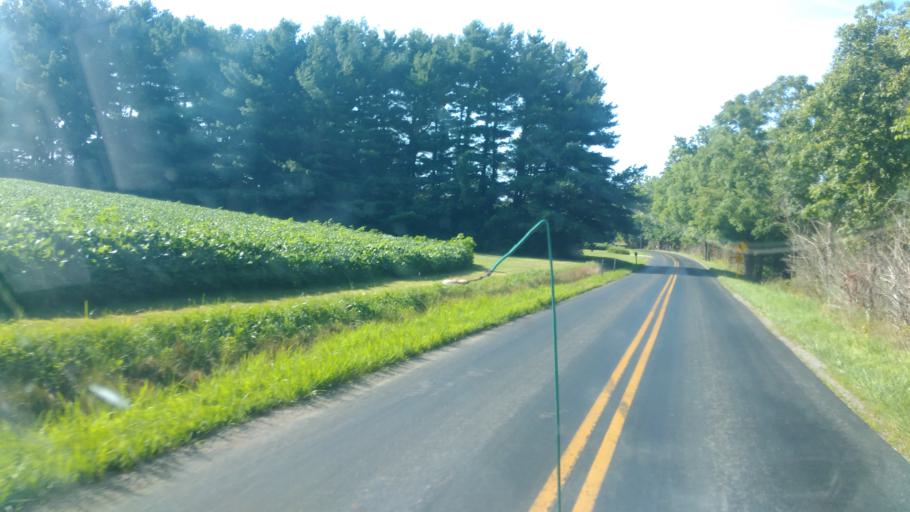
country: US
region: Ohio
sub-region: Delaware County
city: Delaware
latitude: 40.3220
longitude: -83.0687
